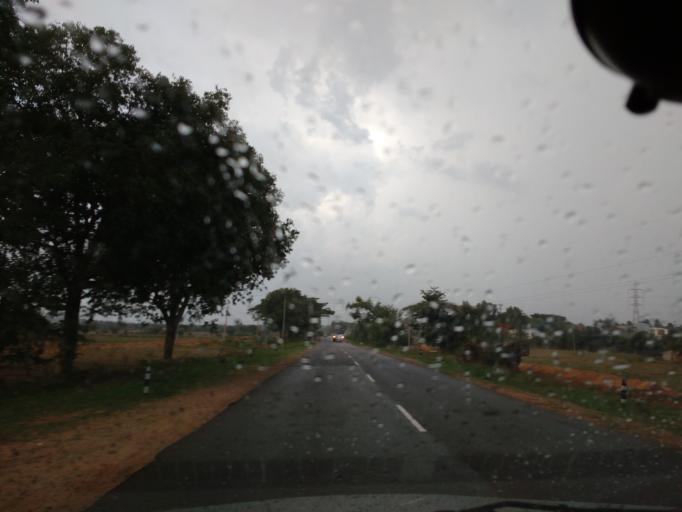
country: IN
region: Karnataka
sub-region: Tumkur
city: Tiptur
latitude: 13.2859
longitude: 76.5649
